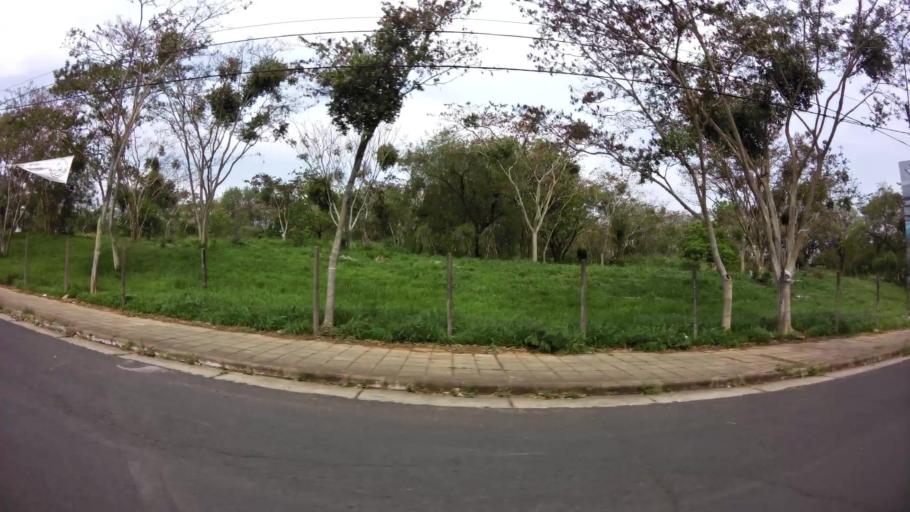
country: PY
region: Asuncion
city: Asuncion
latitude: -25.2784
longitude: -57.5787
